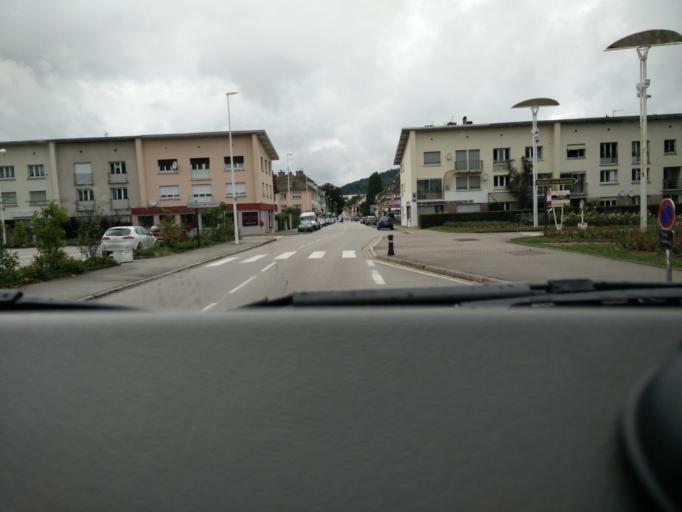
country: FR
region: Lorraine
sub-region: Departement des Vosges
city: Saint-Die-des-Vosges
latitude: 48.2861
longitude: 6.9454
